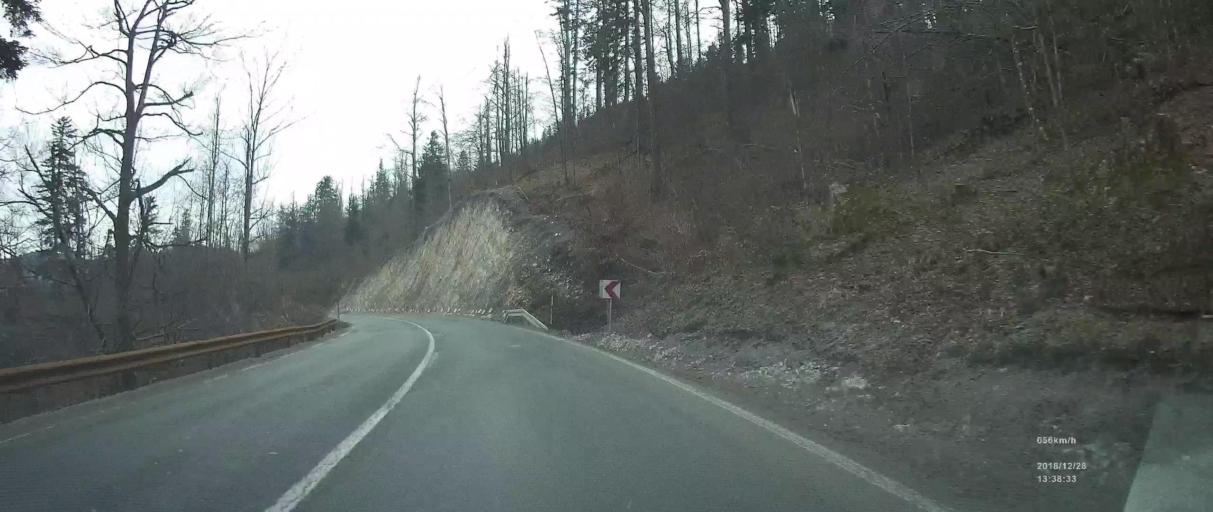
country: HR
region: Primorsko-Goranska
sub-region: Grad Delnice
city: Delnice
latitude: 45.3549
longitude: 14.7257
